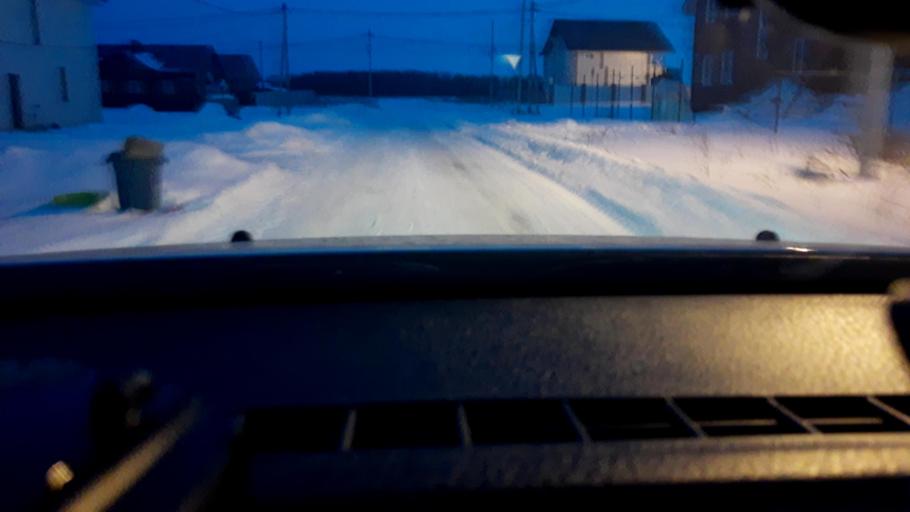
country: RU
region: Bashkortostan
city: Kabakovo
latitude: 54.6093
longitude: 56.1310
